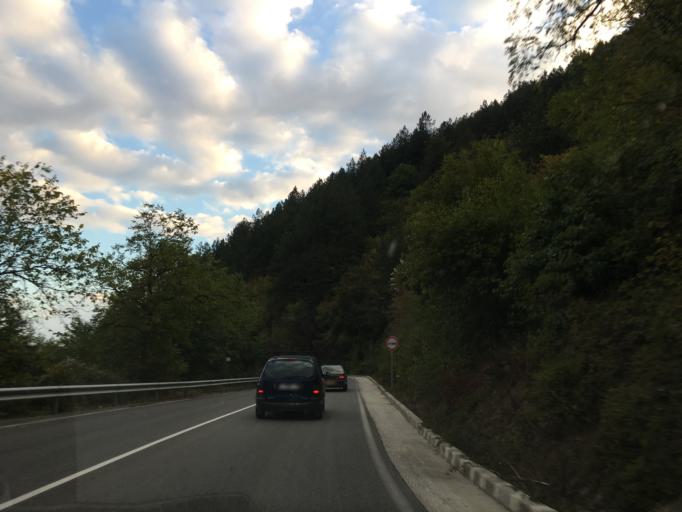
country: BG
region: Sofiya
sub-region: Obshtina Svoge
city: Svoge
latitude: 42.8774
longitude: 23.3753
